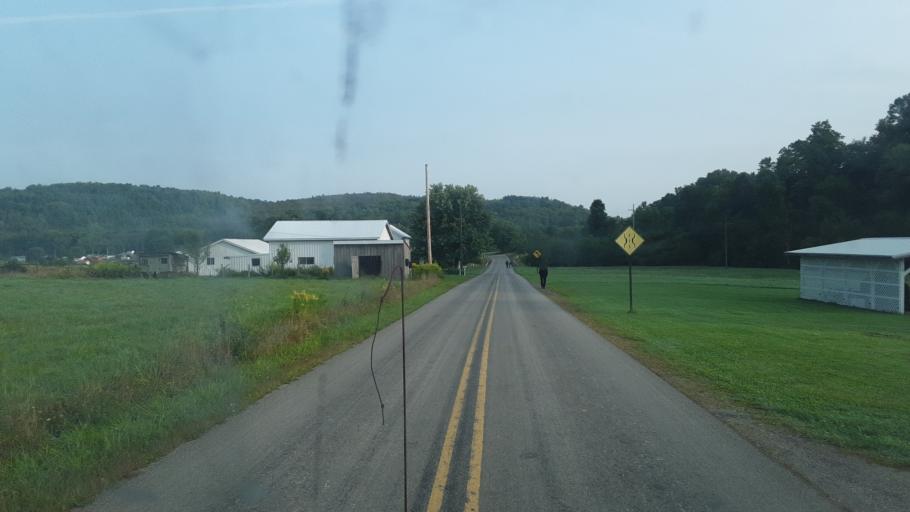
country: US
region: Pennsylvania
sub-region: Jefferson County
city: Punxsutawney
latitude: 40.9602
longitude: -79.1473
